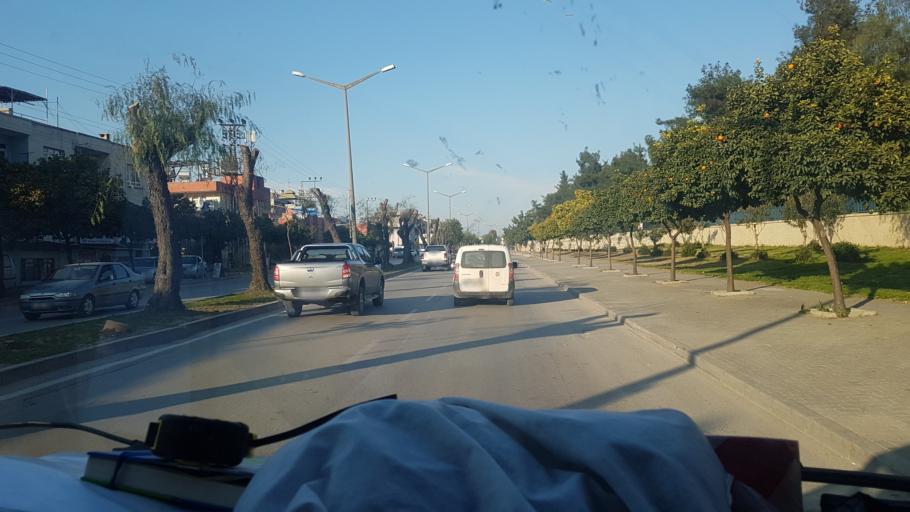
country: TR
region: Adana
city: Adana
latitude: 37.0162
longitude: 35.3400
